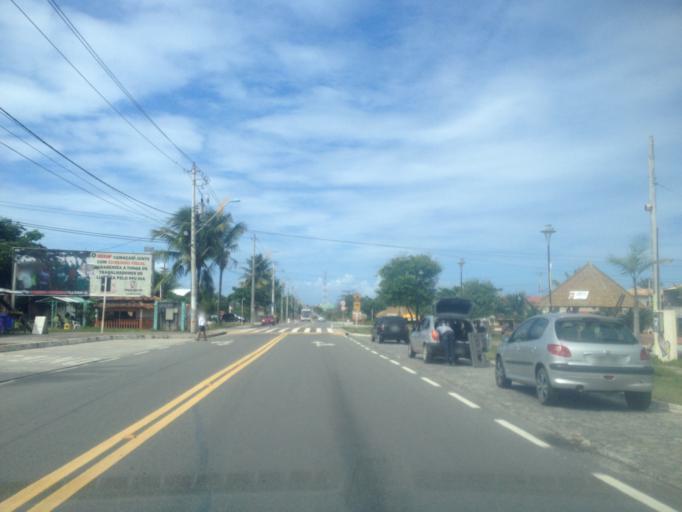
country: BR
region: Bahia
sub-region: Camacari
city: Camacari
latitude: -12.7676
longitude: -38.1865
